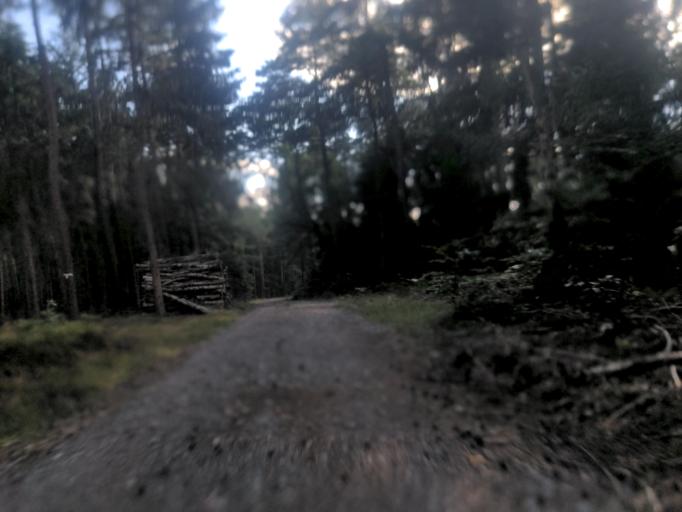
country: DE
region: Lower Saxony
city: Tosterglope
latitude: 53.2043
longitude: 10.8430
